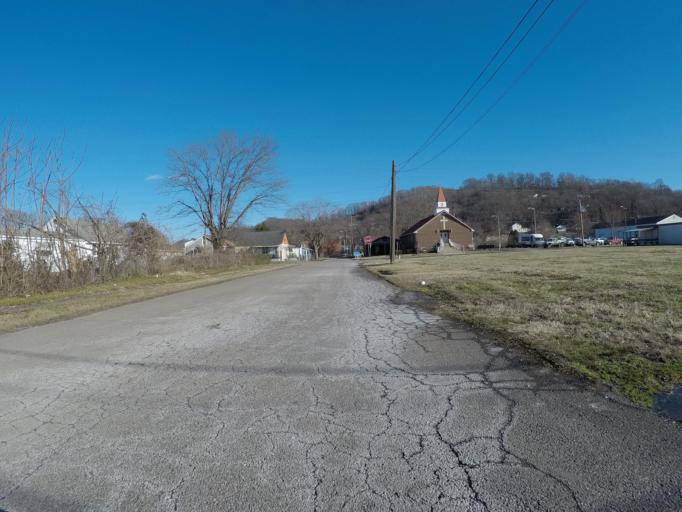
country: US
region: West Virginia
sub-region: Cabell County
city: Huntington
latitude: 38.4265
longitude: -82.3872
